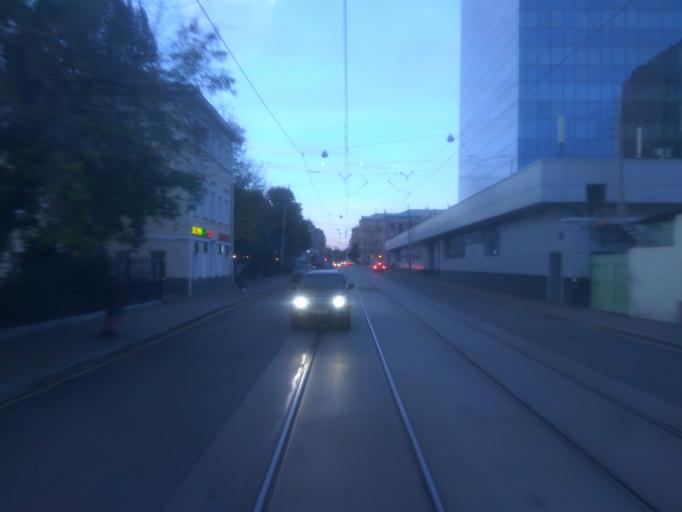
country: RU
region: Moscow
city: Lefortovo
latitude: 55.7672
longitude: 37.6797
